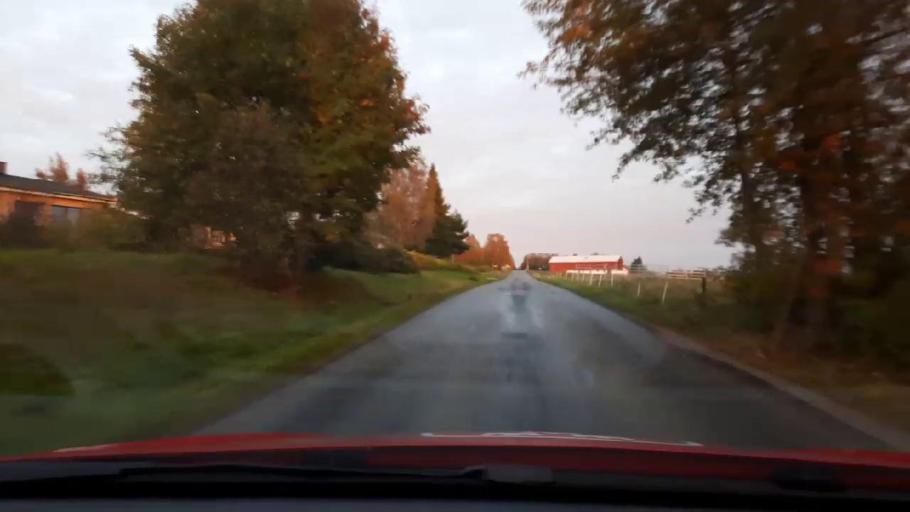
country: SE
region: Jaemtland
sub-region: OEstersunds Kommun
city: Ostersund
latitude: 63.2429
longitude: 14.5482
